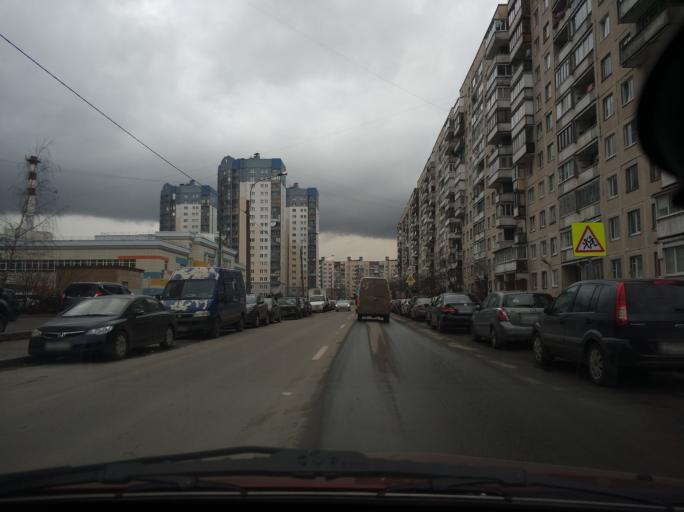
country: RU
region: St.-Petersburg
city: Krasnogvargeisky
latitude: 59.9468
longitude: 30.4838
